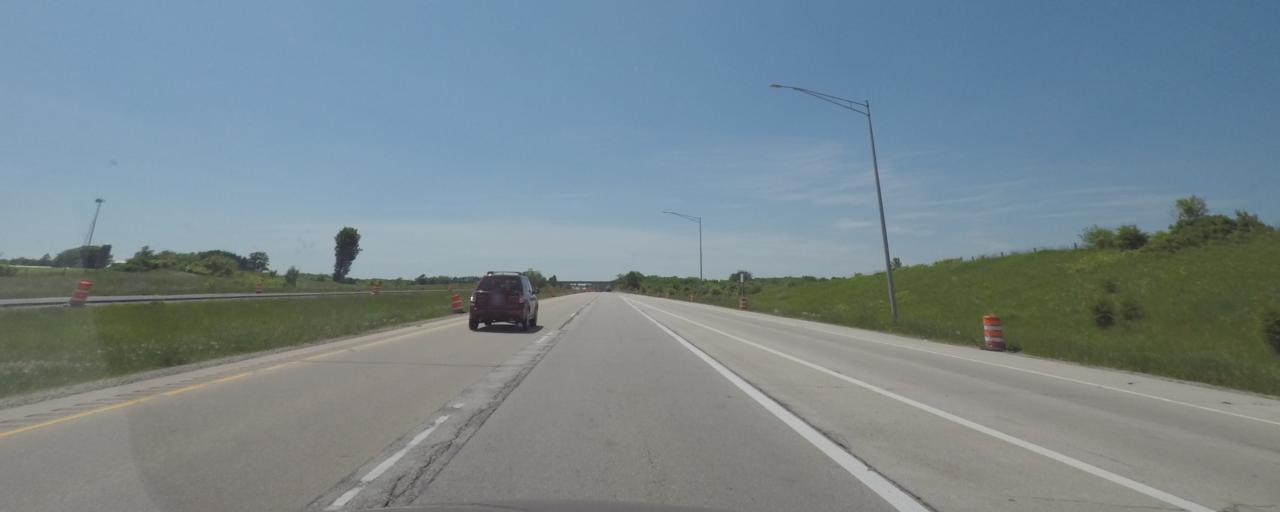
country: US
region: Wisconsin
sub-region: Jefferson County
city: Johnson Creek
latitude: 43.0867
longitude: -88.8286
